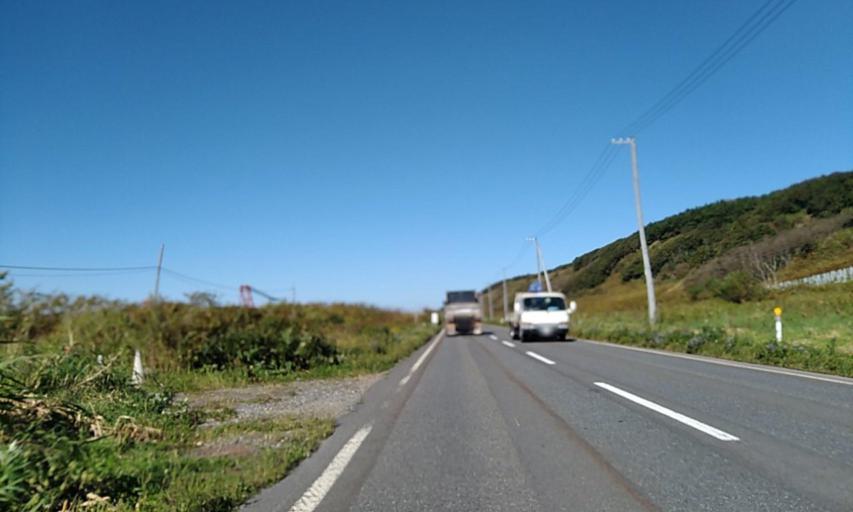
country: JP
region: Hokkaido
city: Shizunai-furukawacho
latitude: 42.4637
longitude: 142.1566
